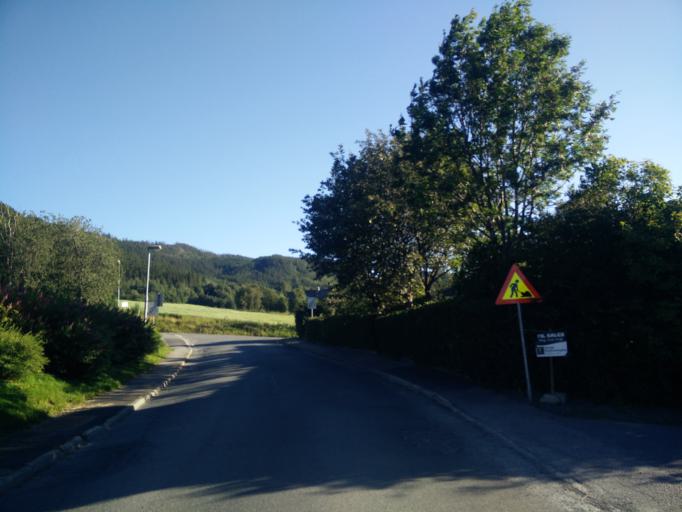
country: NO
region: Sor-Trondelag
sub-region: Malvik
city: Malvik
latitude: 63.4313
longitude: 10.5839
